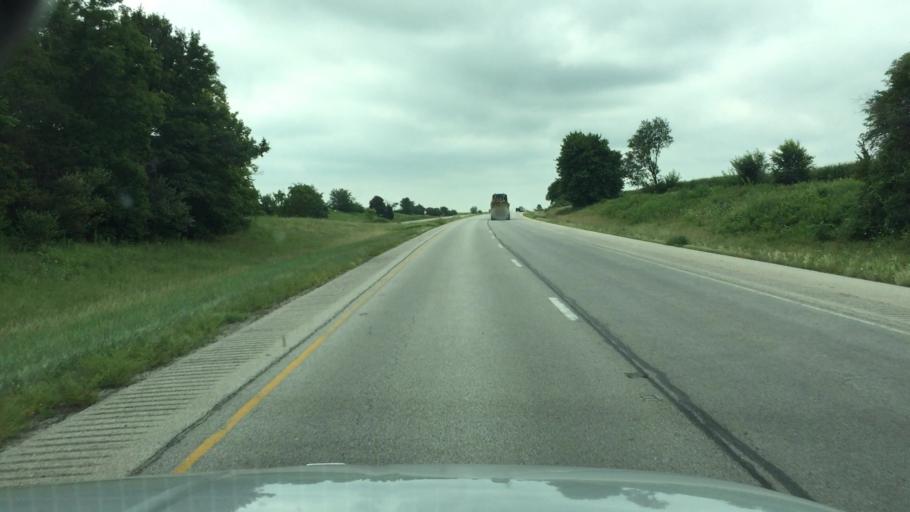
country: US
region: Illinois
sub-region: Knox County
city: Galesburg
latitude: 41.0631
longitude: -90.3338
